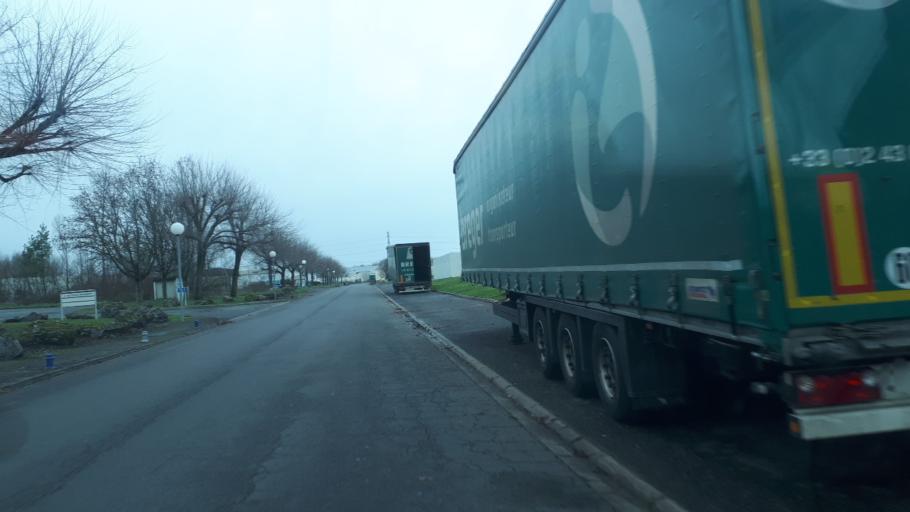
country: FR
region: Centre
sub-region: Departement du Loir-et-Cher
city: Romorantin-Lanthenay
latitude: 47.3365
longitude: 1.7477
